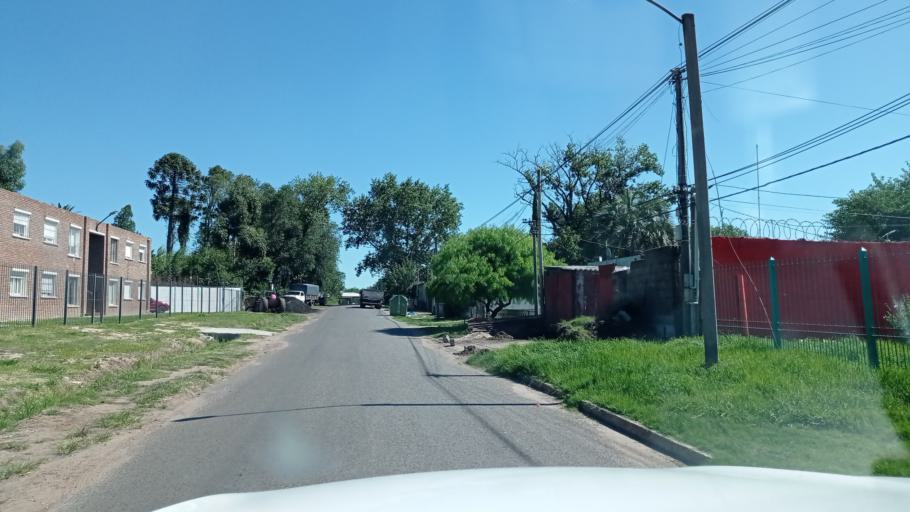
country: UY
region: Canelones
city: La Paz
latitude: -34.8310
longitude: -56.2398
